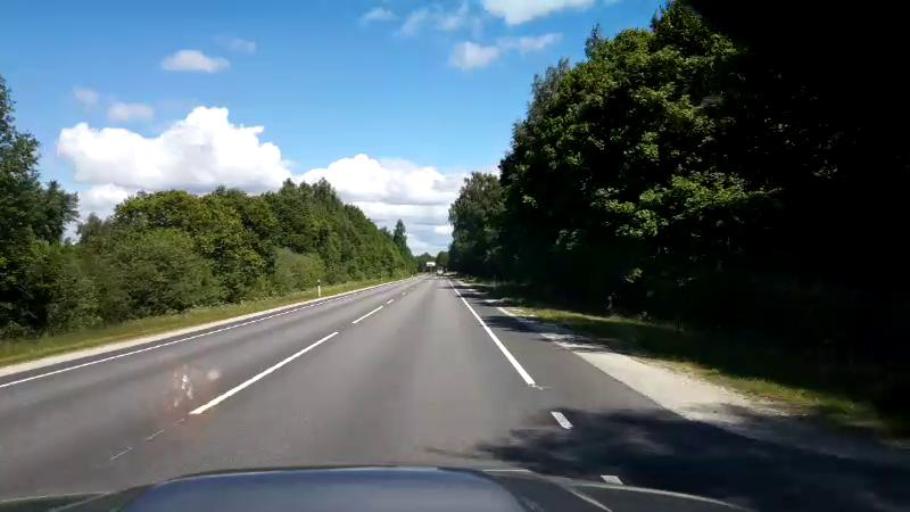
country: EE
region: Paernumaa
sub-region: Paernu linn
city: Parnu
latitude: 58.2291
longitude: 24.4995
